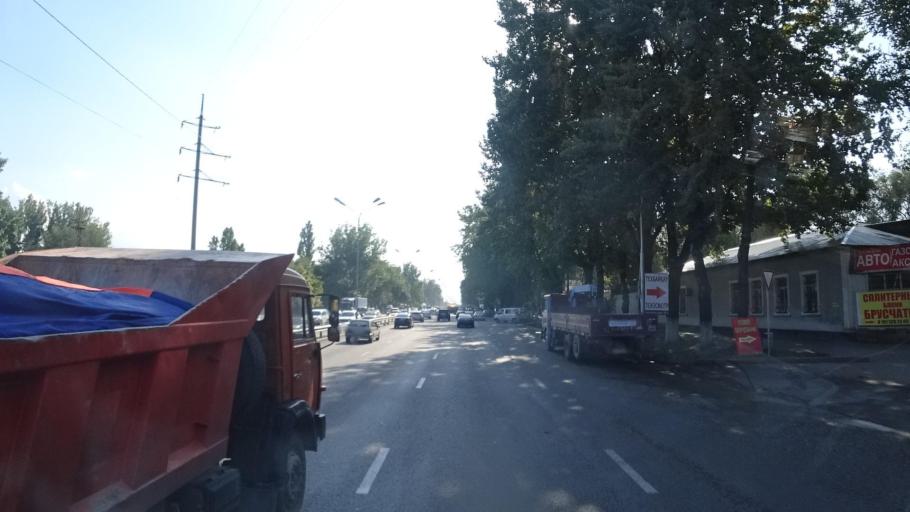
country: KZ
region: Almaty Qalasy
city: Almaty
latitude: 43.2895
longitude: 76.9260
